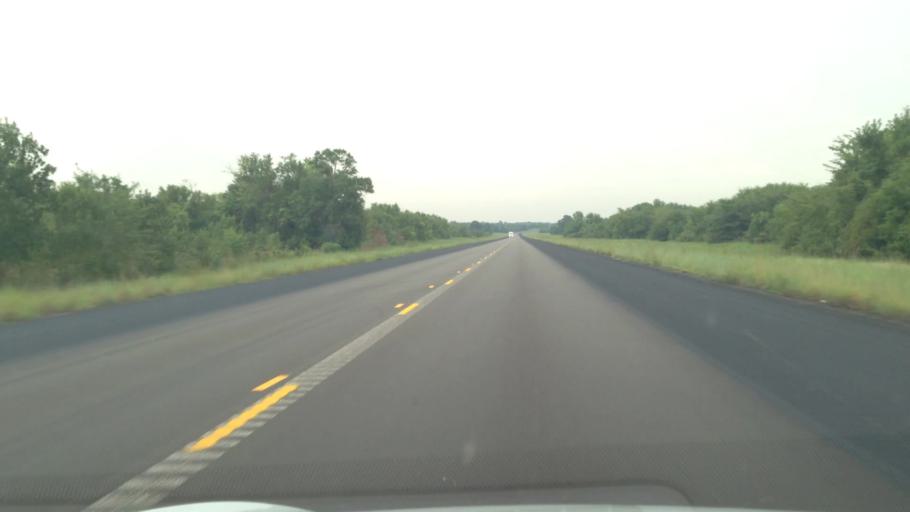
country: US
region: Kansas
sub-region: Cherokee County
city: Baxter Springs
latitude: 37.0395
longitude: -94.7092
